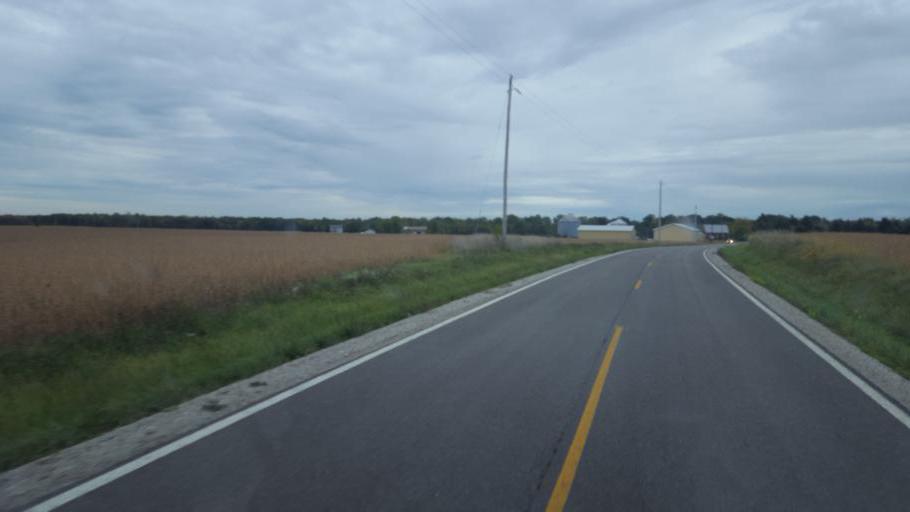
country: US
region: Ohio
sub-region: Huron County
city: New London
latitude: 41.1401
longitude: -82.4159
